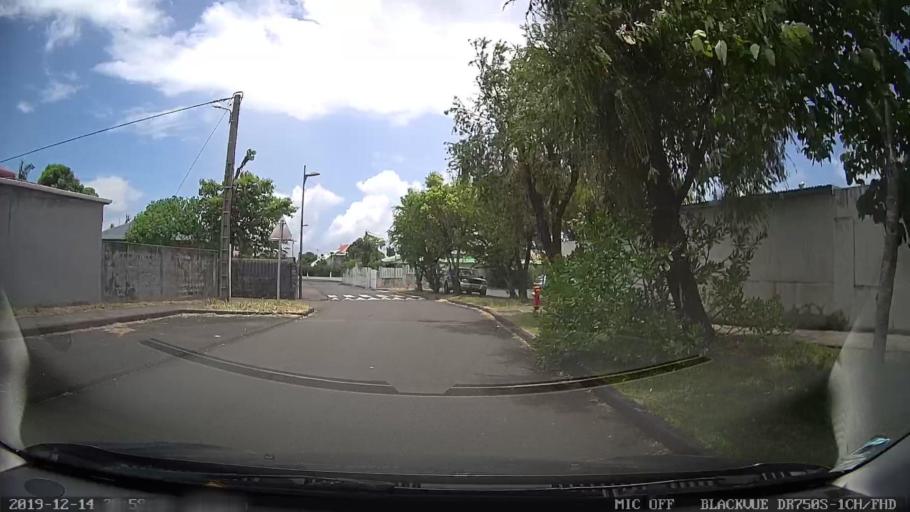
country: RE
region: Reunion
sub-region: Reunion
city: Saint-Andre
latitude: -20.9709
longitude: 55.6572
